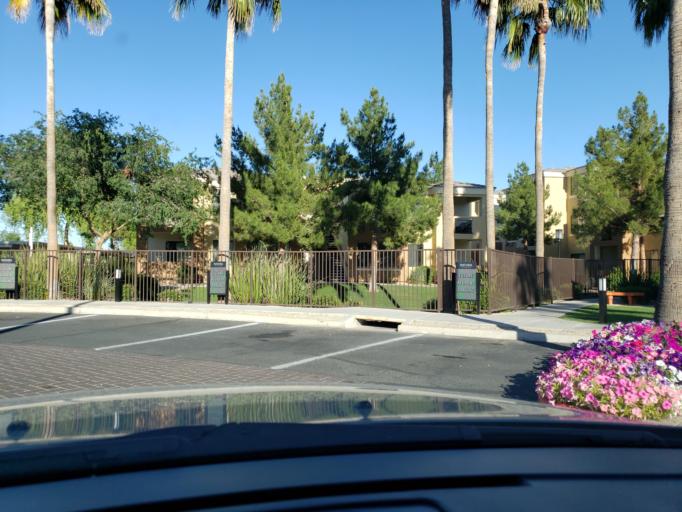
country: US
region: Arizona
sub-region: Maricopa County
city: Youngtown
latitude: 33.5651
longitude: -112.2930
